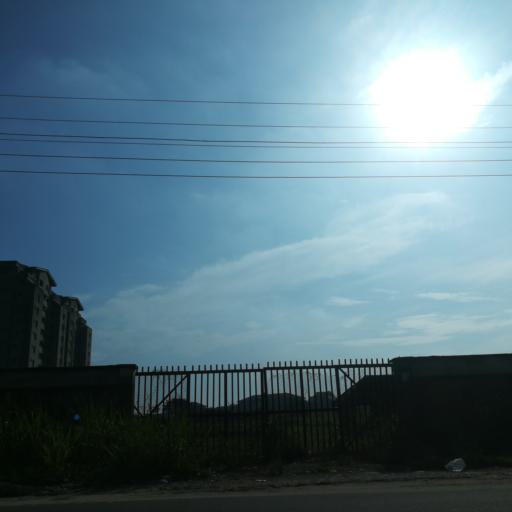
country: NG
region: Rivers
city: Port Harcourt
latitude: 4.7988
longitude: 7.0270
